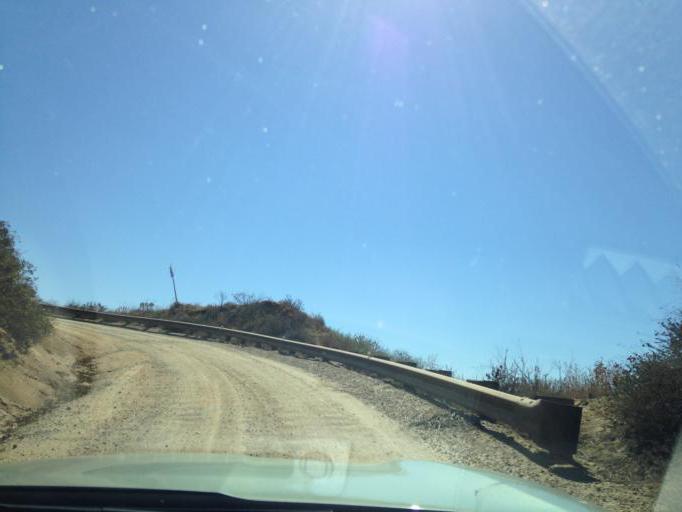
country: US
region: California
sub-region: San Bernardino County
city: Mentone
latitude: 34.1119
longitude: -117.1281
